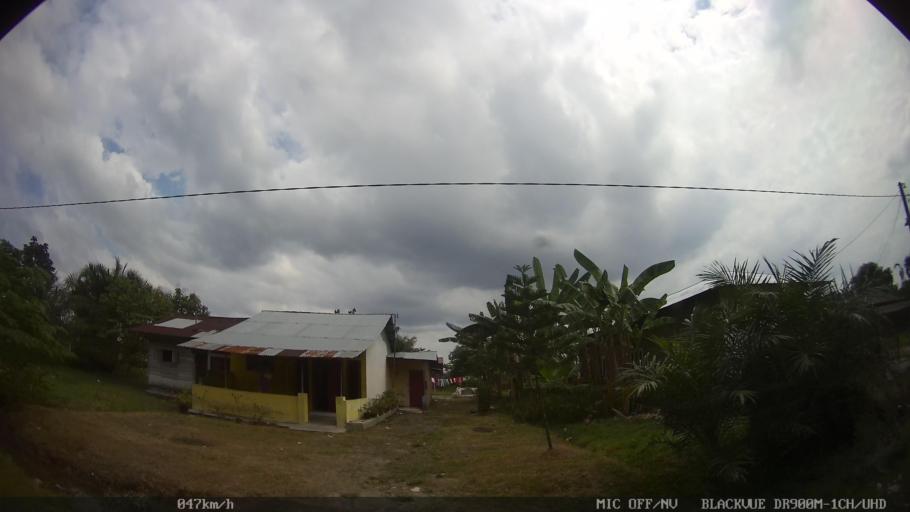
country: ID
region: North Sumatra
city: Sunggal
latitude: 3.6355
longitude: 98.6035
